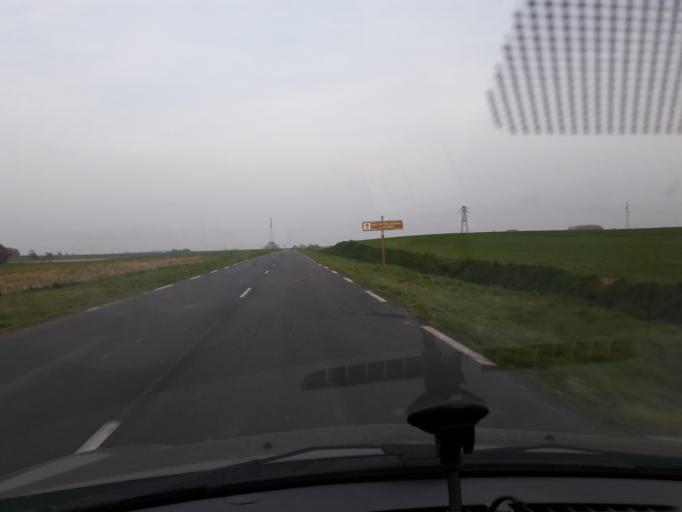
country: FR
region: Nord-Pas-de-Calais
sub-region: Departement du Nord
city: Recquignies
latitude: 50.2584
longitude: 4.0381
